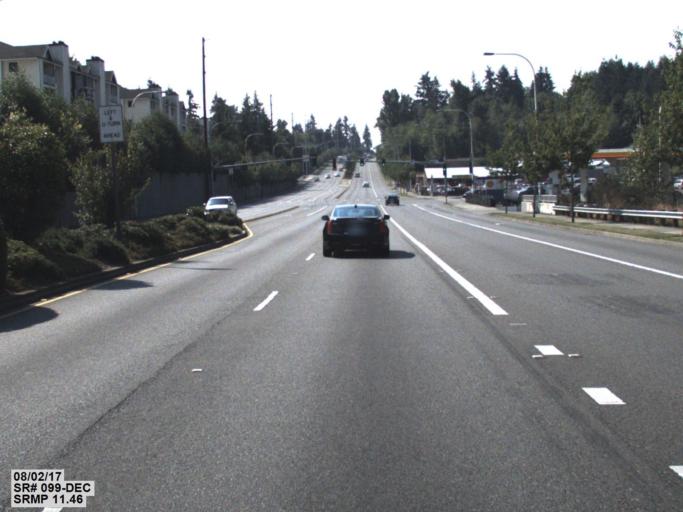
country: US
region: Washington
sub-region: King County
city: Federal Way
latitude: 47.3371
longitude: -122.3123
